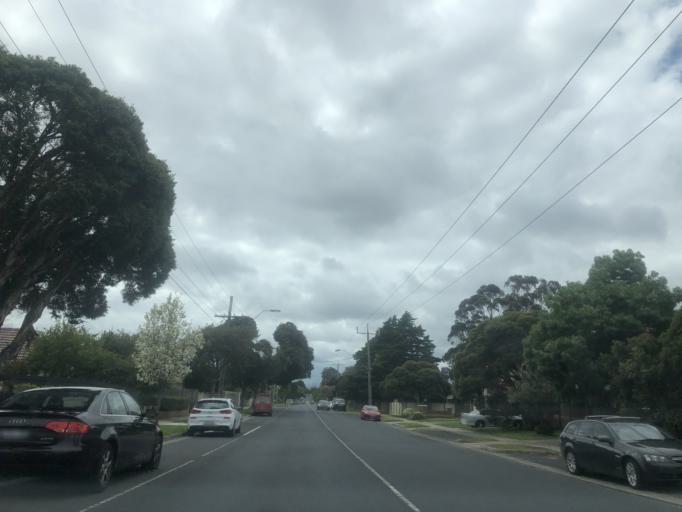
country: AU
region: Victoria
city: Murrumbeena
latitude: -37.9073
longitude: 145.0744
